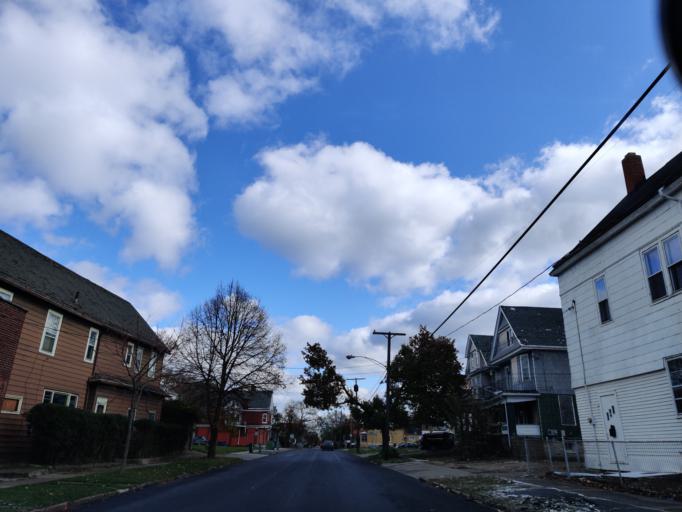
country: US
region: New York
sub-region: Erie County
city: Buffalo
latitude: 42.9220
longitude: -78.8926
